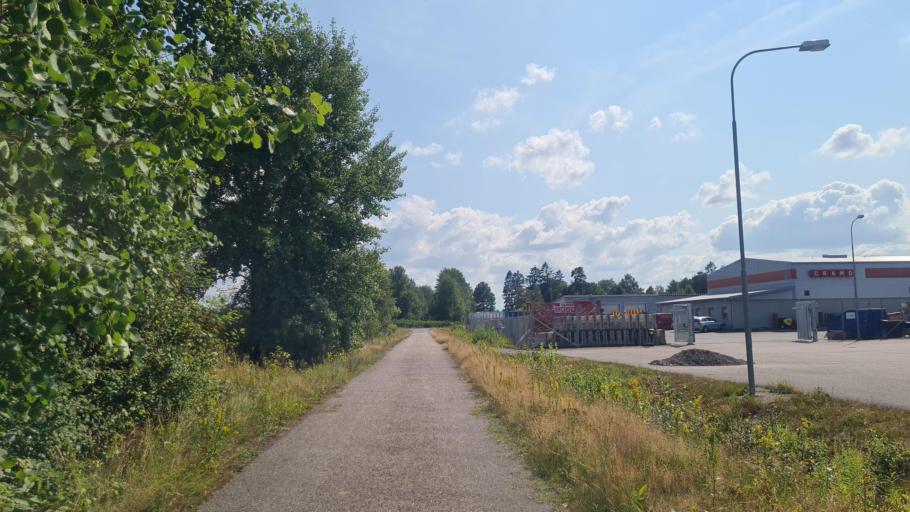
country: SE
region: Kronoberg
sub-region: Ljungby Kommun
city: Ljungby
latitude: 56.8154
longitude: 13.9187
